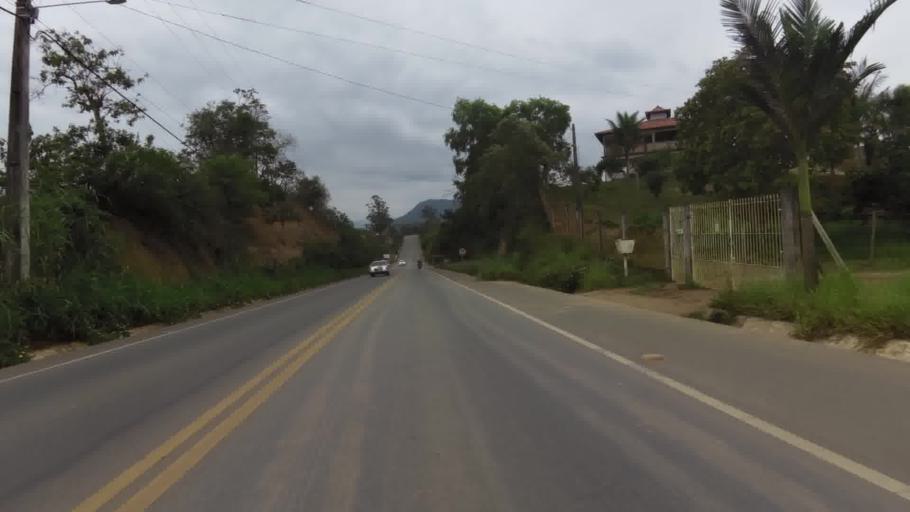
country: BR
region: Espirito Santo
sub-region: Piuma
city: Piuma
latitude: -20.8180
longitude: -40.7335
